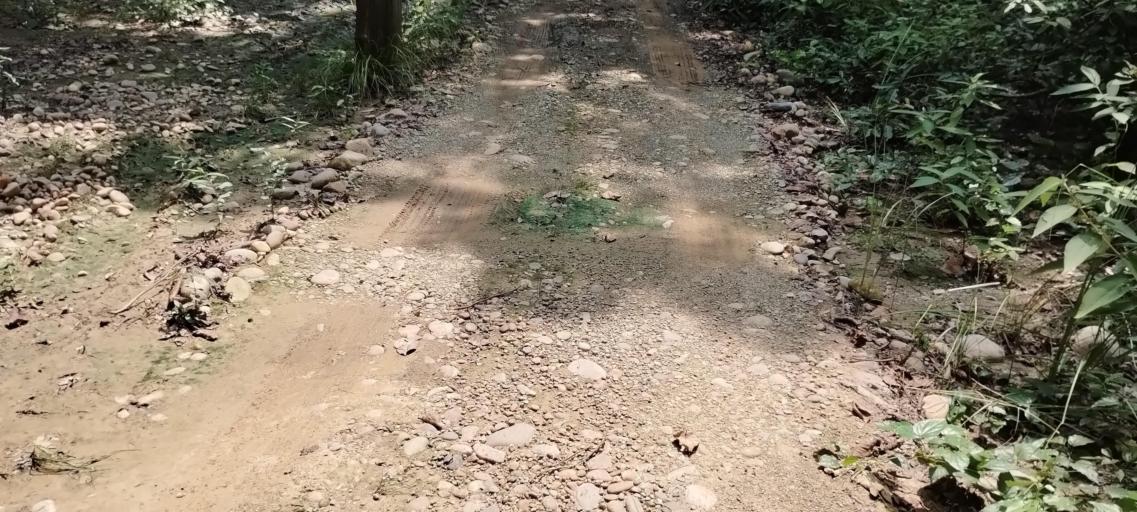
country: NP
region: Far Western
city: Tikapur
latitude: 28.4979
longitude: 81.2560
